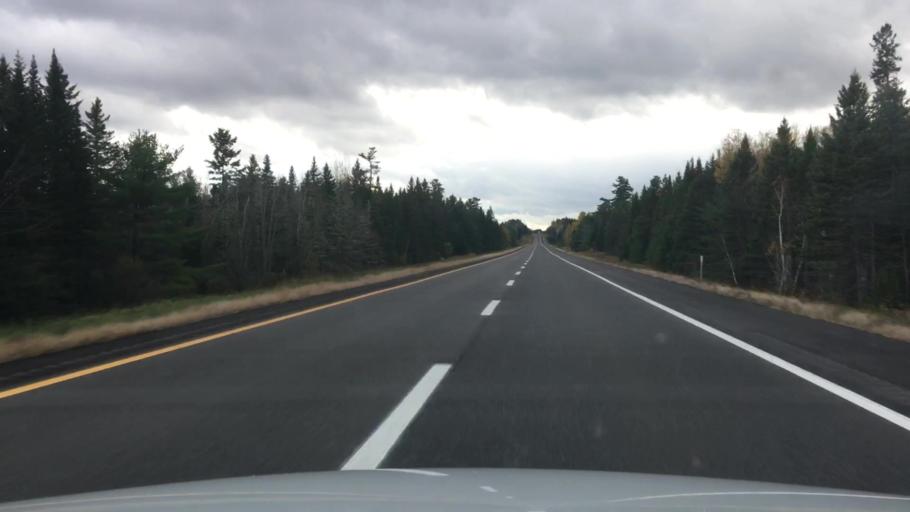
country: US
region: Maine
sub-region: Penobscot County
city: Patten
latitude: 46.0712
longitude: -68.2234
